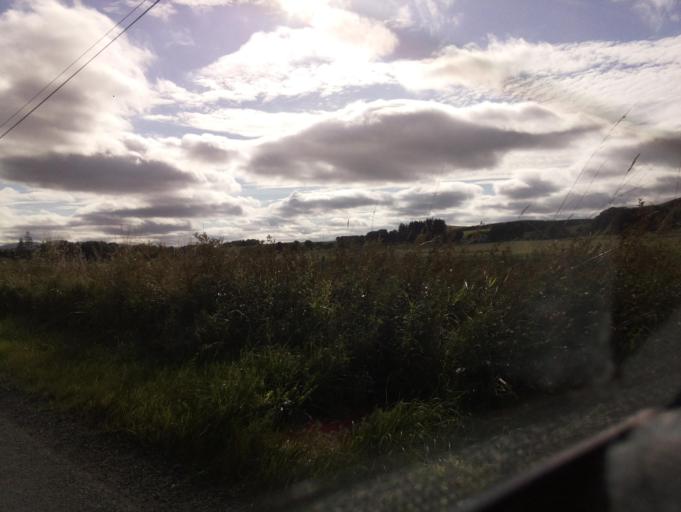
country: GB
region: Scotland
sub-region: South Lanarkshire
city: Biggar
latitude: 55.6570
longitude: -3.4317
